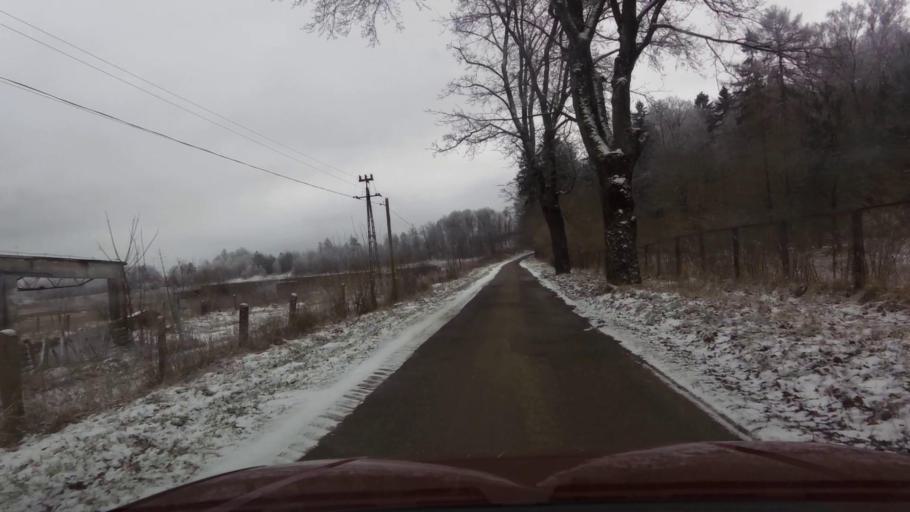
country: PL
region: West Pomeranian Voivodeship
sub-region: Powiat swidwinski
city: Polczyn-Zdroj
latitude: 53.7879
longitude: 16.0399
